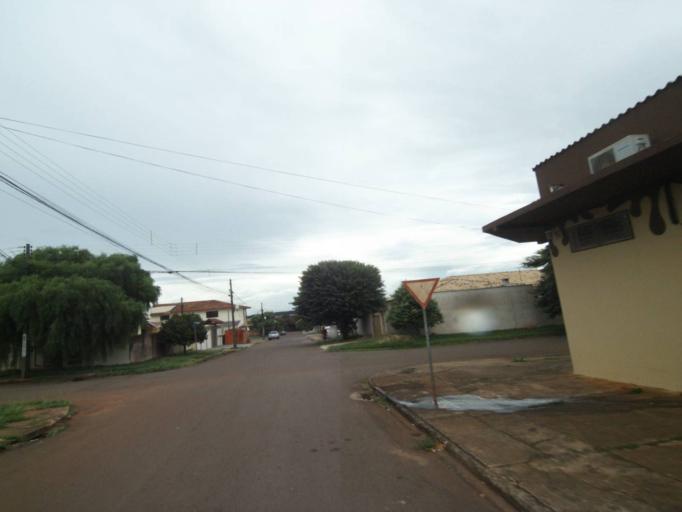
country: BR
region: Parana
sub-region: Campo Mourao
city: Campo Mourao
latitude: -24.0283
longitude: -52.3591
